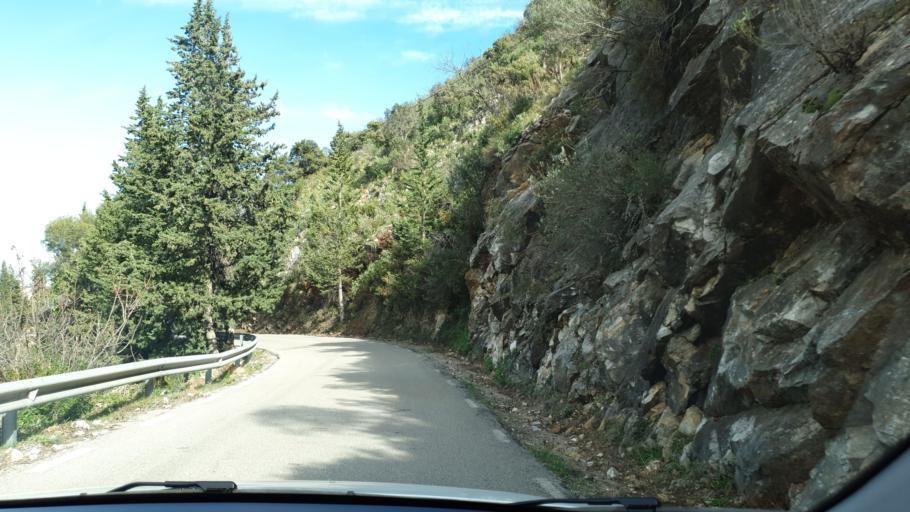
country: ES
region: Andalusia
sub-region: Provincia de Malaga
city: Ojen
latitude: 36.5895
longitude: -4.8778
